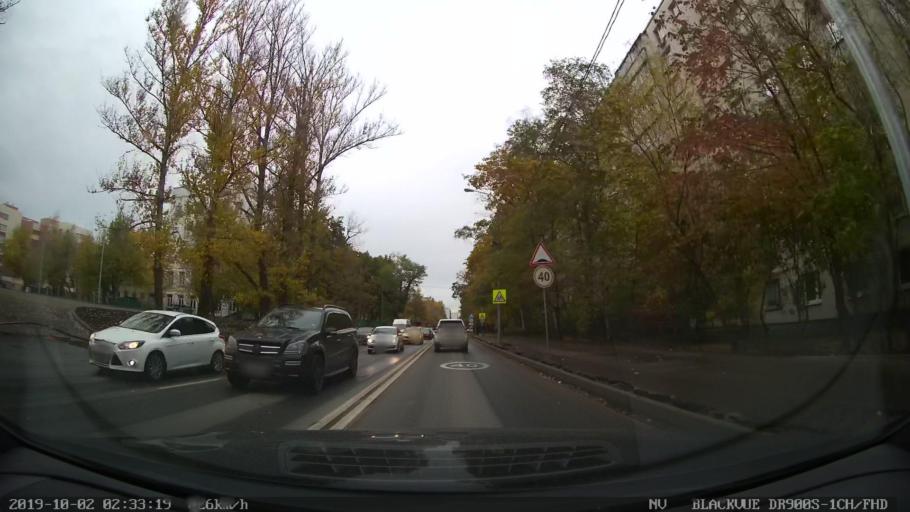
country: RU
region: Moscow
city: Novovladykino
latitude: 55.8135
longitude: 37.5825
